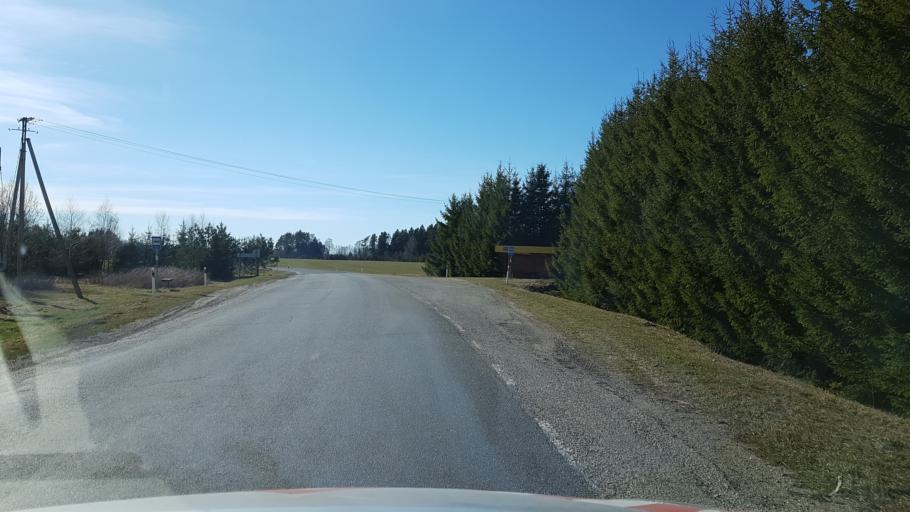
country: EE
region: Laeaene-Virumaa
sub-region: Vinni vald
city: Vinni
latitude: 59.3052
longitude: 26.5655
